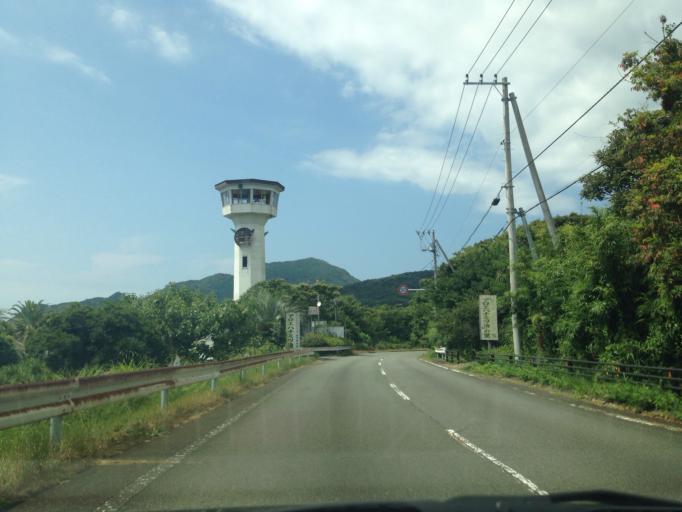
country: JP
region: Shizuoka
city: Shimoda
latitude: 34.6875
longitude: 138.7732
